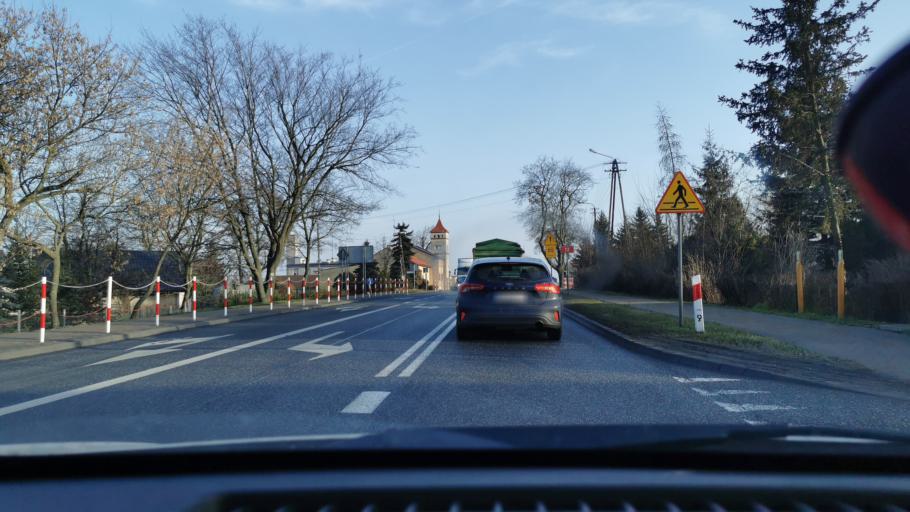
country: PL
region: Lodz Voivodeship
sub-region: Powiat sieradzki
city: Wroblew
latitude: 51.6120
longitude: 18.6152
